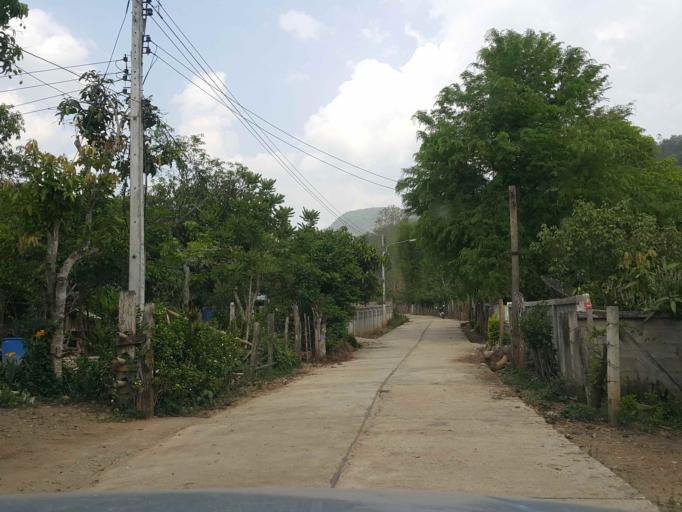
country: TH
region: Chiang Mai
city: Wiang Haeng
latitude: 19.3966
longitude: 98.7225
